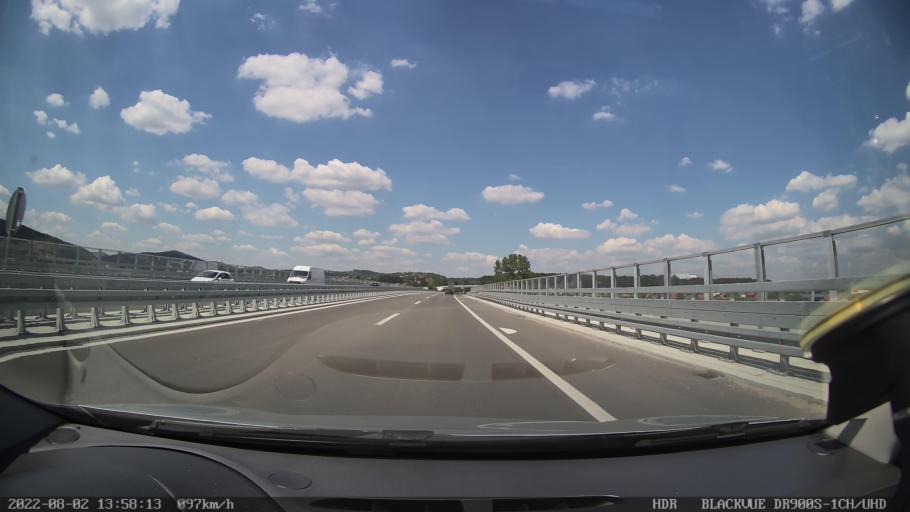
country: RS
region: Central Serbia
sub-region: Moravicki Okrug
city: Cacak
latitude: 43.9068
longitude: 20.2735
